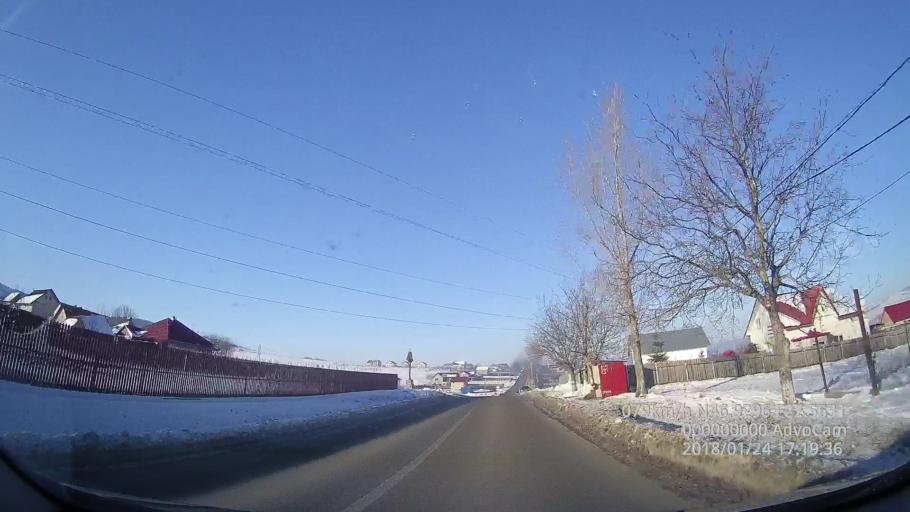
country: RO
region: Iasi
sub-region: Comuna Scanteia
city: Scanteia
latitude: 46.9303
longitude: 27.5630
